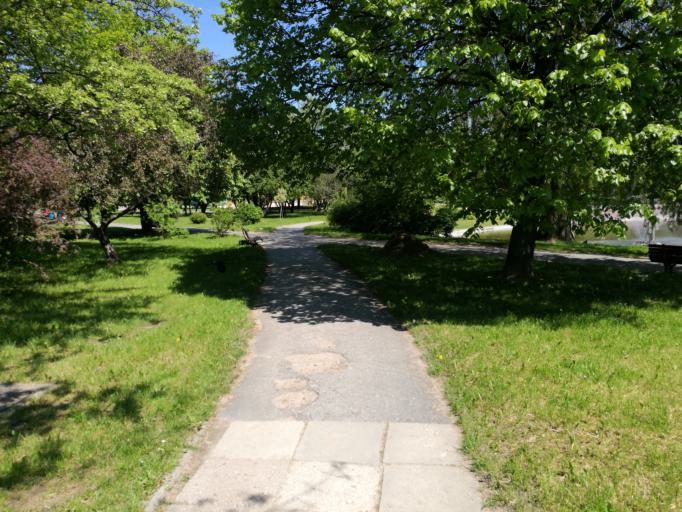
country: PL
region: Swietokrzyskie
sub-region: Powiat kielecki
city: Kielce
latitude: 50.8641
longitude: 20.6417
